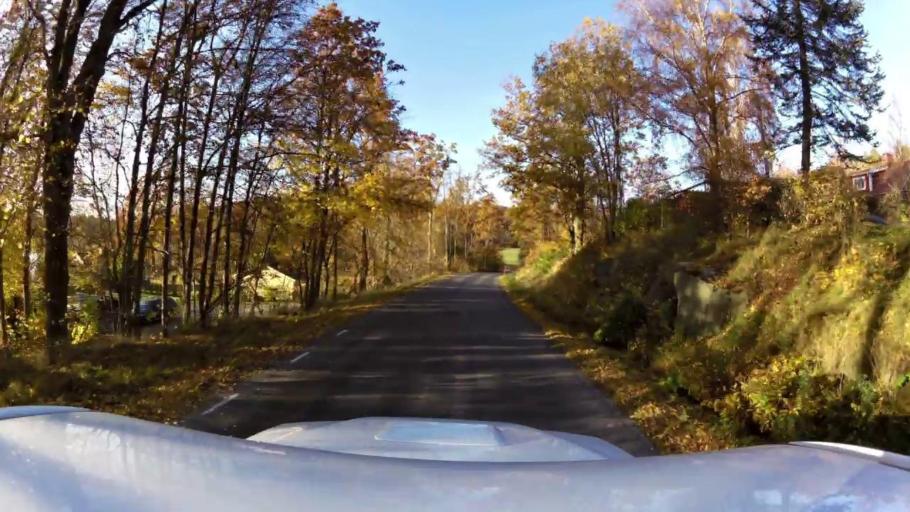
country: SE
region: OEstergoetland
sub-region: Kinda Kommun
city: Rimforsa
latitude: 58.1715
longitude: 15.6887
